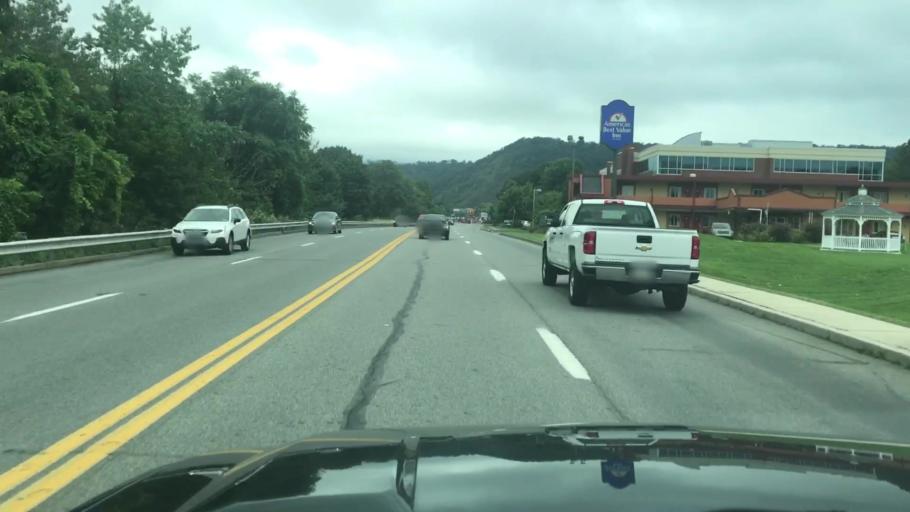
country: US
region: Pennsylvania
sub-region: Perry County
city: Marysville
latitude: 40.3201
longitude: -76.8985
